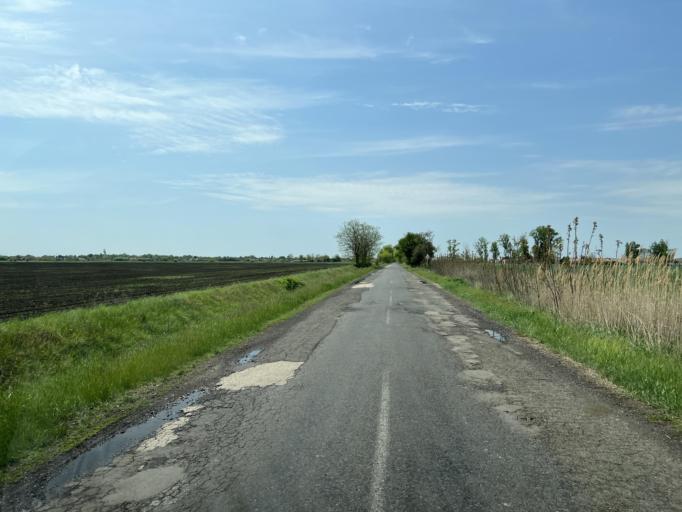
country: HU
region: Pest
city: Tapiogyorgye
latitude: 47.3517
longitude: 19.9598
